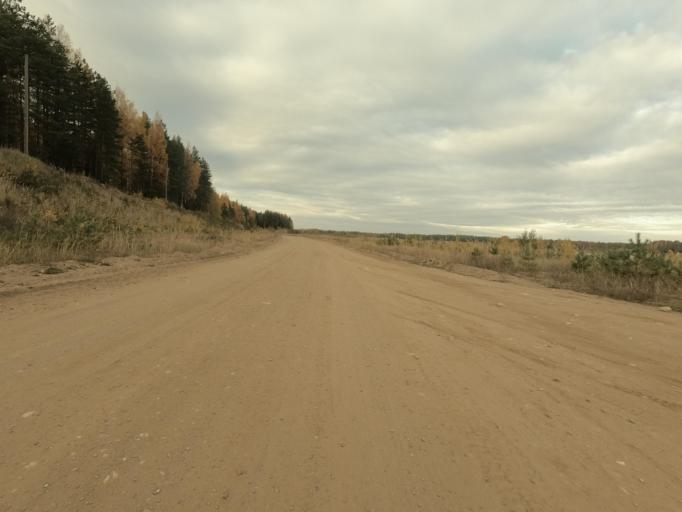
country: RU
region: Leningrad
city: Priladozhskiy
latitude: 59.7003
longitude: 31.3627
